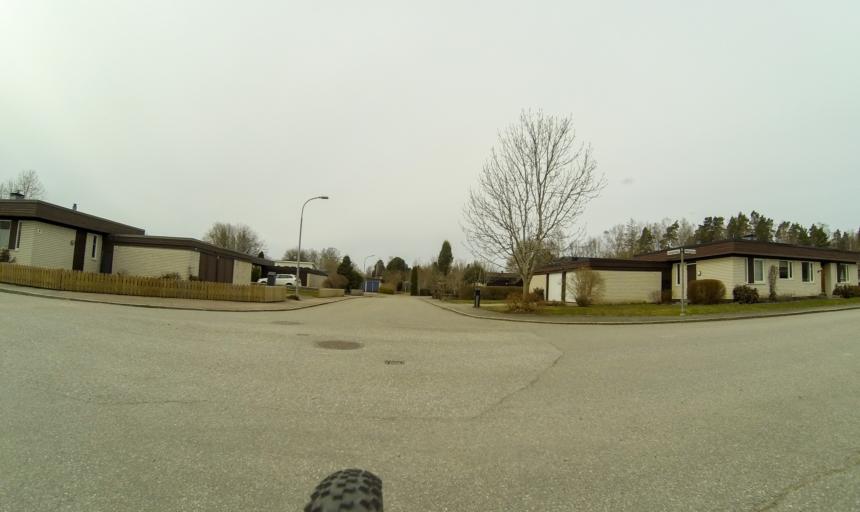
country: SE
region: Vaestmanland
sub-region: Vasteras
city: Vasteras
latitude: 59.5939
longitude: 16.6038
